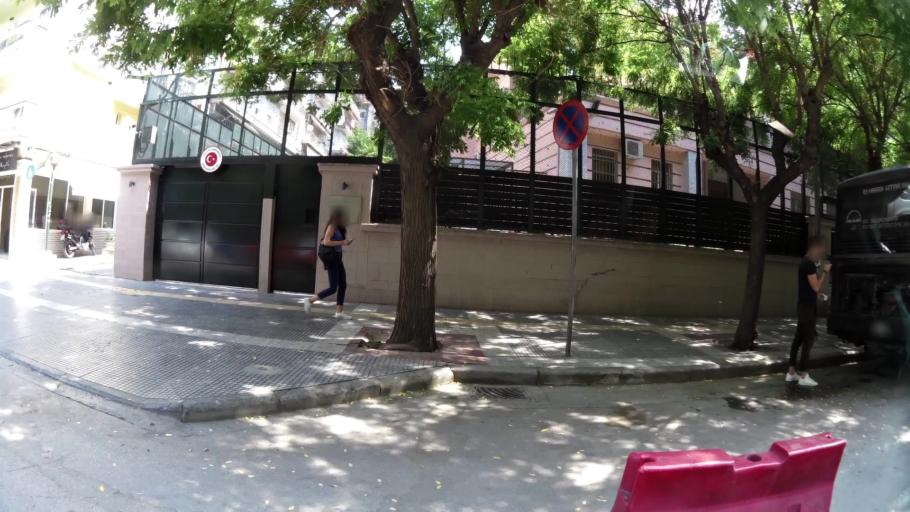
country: GR
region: Central Macedonia
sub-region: Nomos Thessalonikis
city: Agios Pavlos
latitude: 40.6355
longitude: 22.9539
